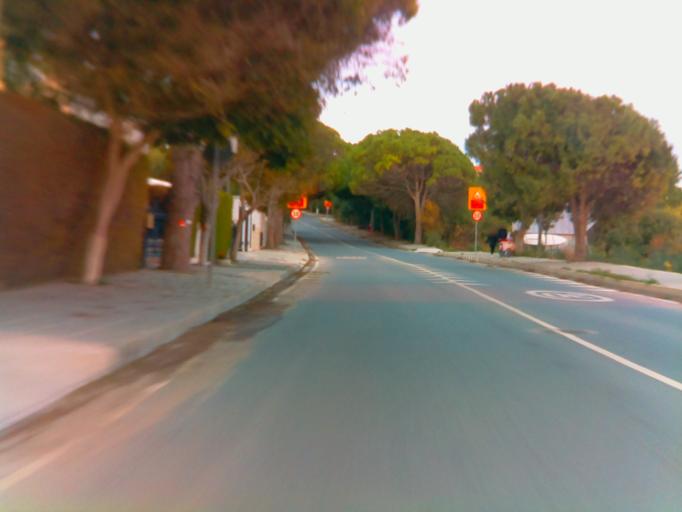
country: CY
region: Pafos
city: Pegeia
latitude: 34.8546
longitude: 32.3708
